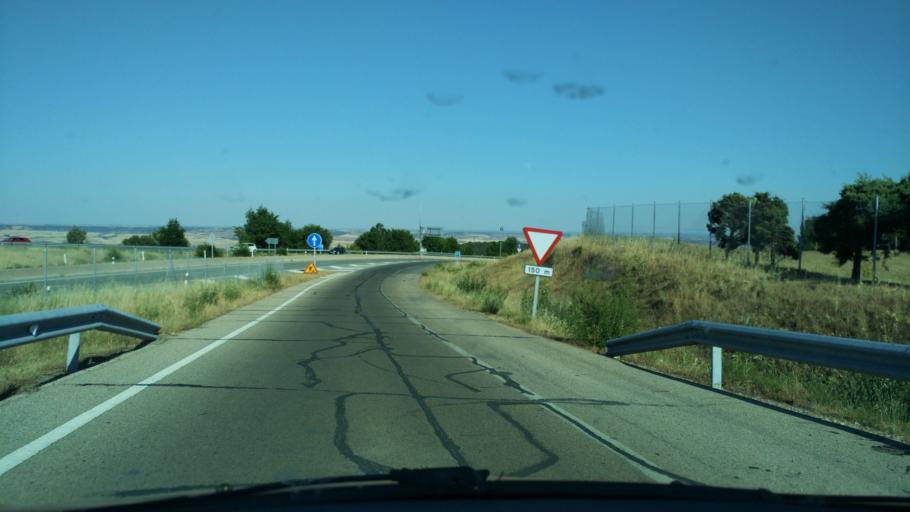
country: ES
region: Madrid
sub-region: Provincia de Madrid
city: Pedrezuela
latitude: 40.7441
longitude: -3.5919
